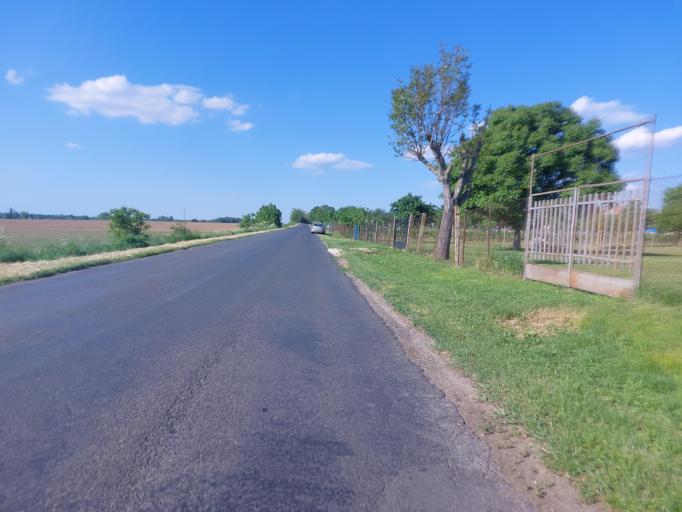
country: HU
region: Veszprem
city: Devecser
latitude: 47.1519
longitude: 17.3564
